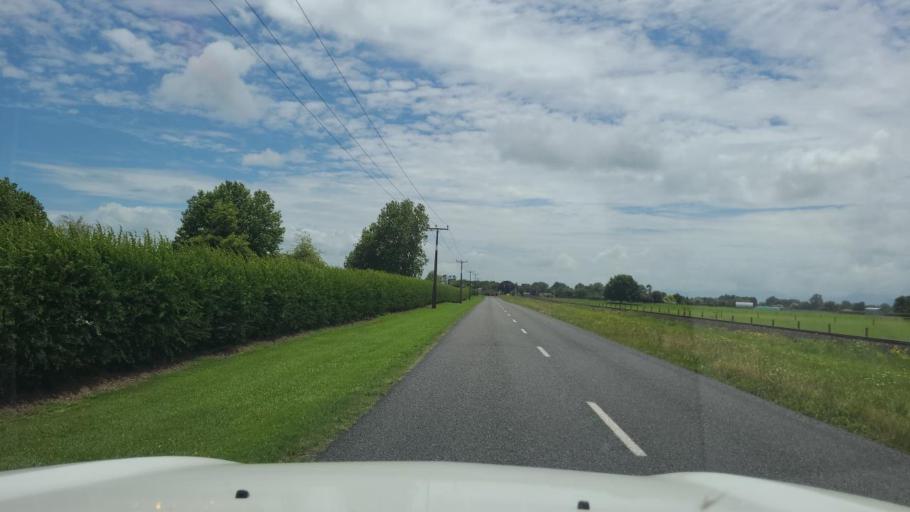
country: NZ
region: Waikato
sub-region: Matamata-Piako District
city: Matamata
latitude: -37.8676
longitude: 175.7554
